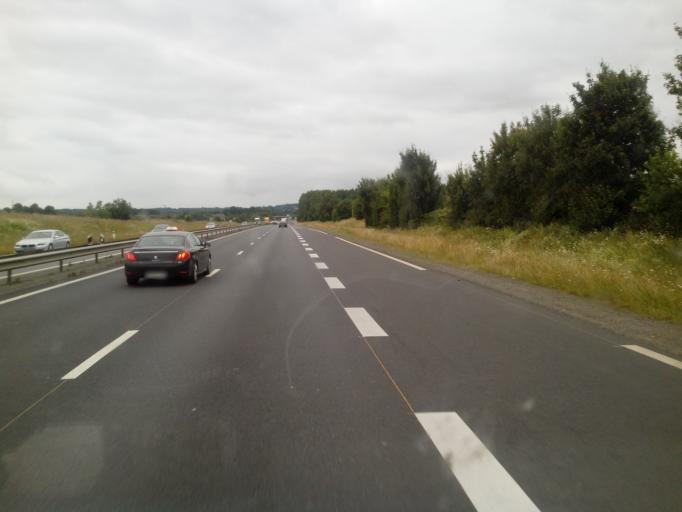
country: FR
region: Brittany
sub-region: Departement d'Ille-et-Vilaine
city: Chartres-de-Bretagne
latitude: 48.0159
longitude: -1.6914
